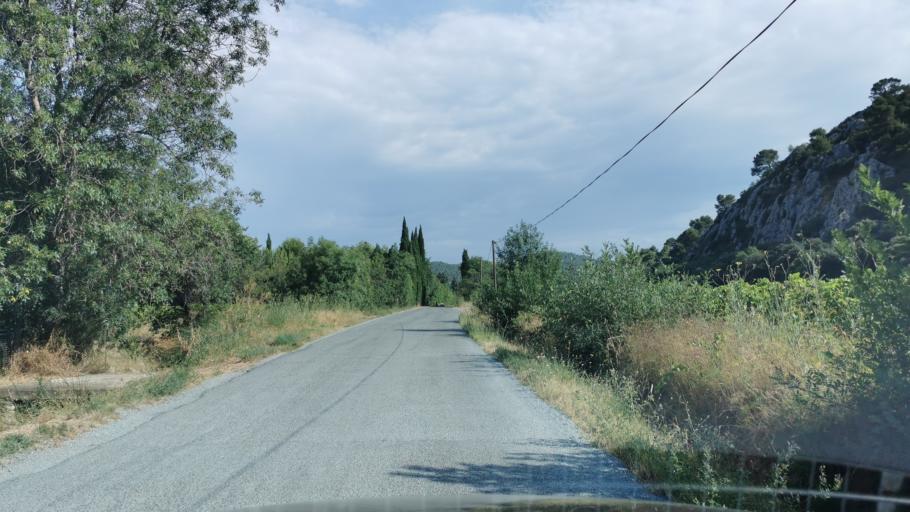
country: FR
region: Languedoc-Roussillon
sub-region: Departement de l'Aude
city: Bize-Minervois
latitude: 43.3329
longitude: 2.8769
